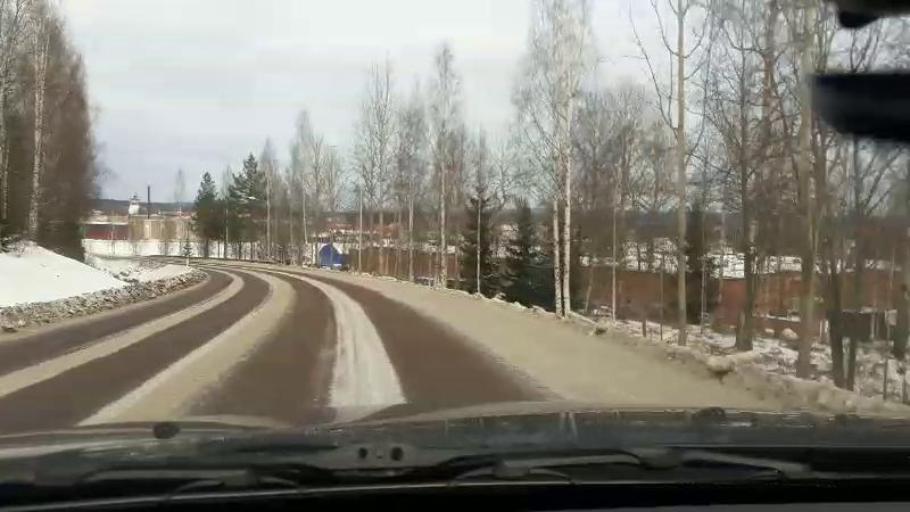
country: SE
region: Gaevleborg
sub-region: Bollnas Kommun
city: Bollnas
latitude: 61.3349
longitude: 16.3928
